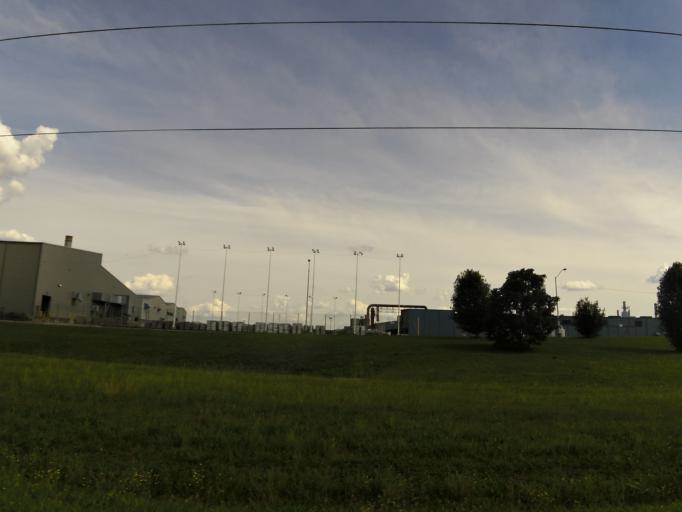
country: US
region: Tennessee
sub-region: Carroll County
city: Huntingdon
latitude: 36.0197
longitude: -88.3846
